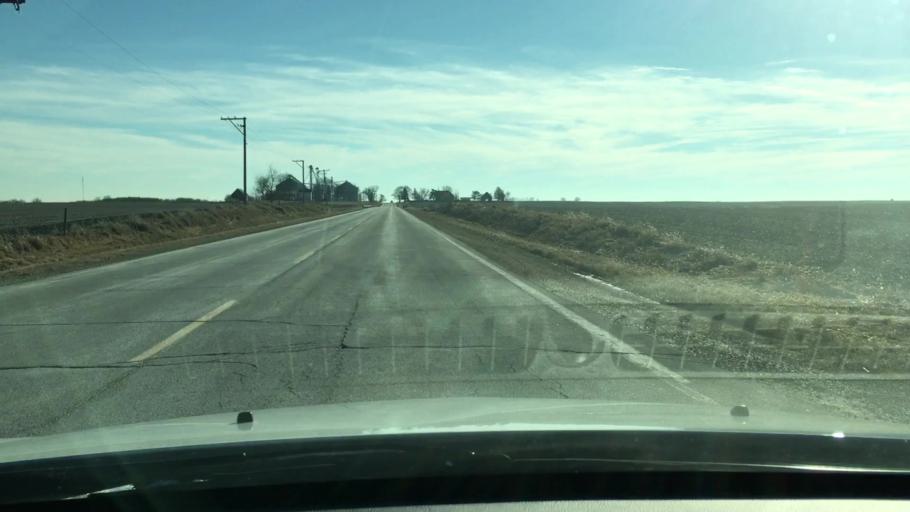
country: US
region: Illinois
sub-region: LaSalle County
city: Mendota
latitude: 41.5987
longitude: -89.1285
